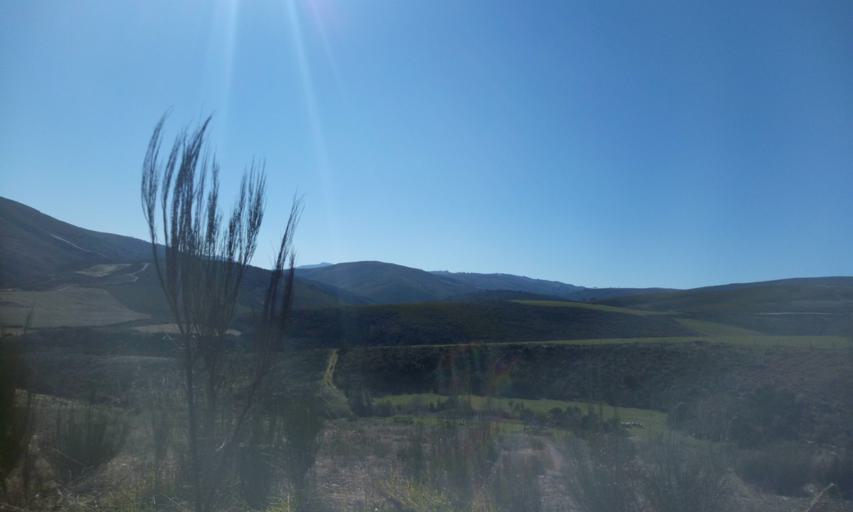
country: PT
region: Guarda
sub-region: Manteigas
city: Manteigas
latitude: 40.4616
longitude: -7.4976
